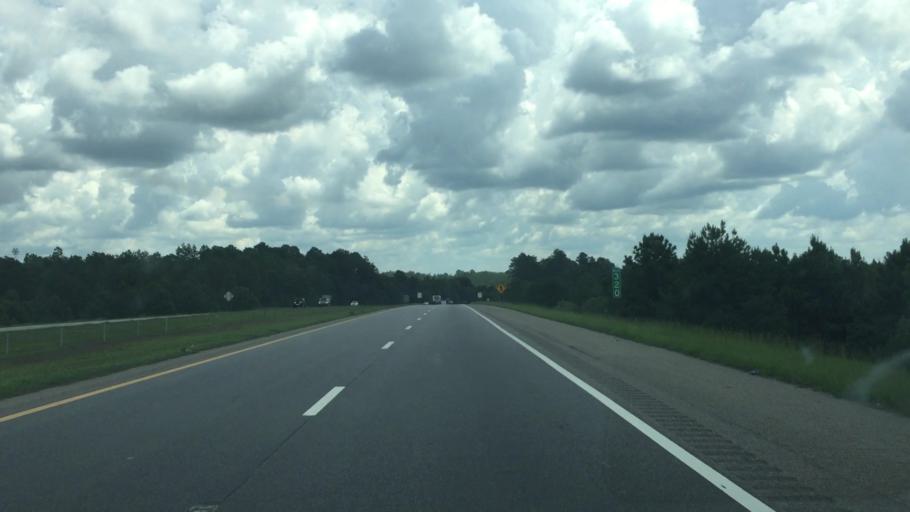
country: US
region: North Carolina
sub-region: Richmond County
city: Hamlet
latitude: 34.8641
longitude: -79.6702
